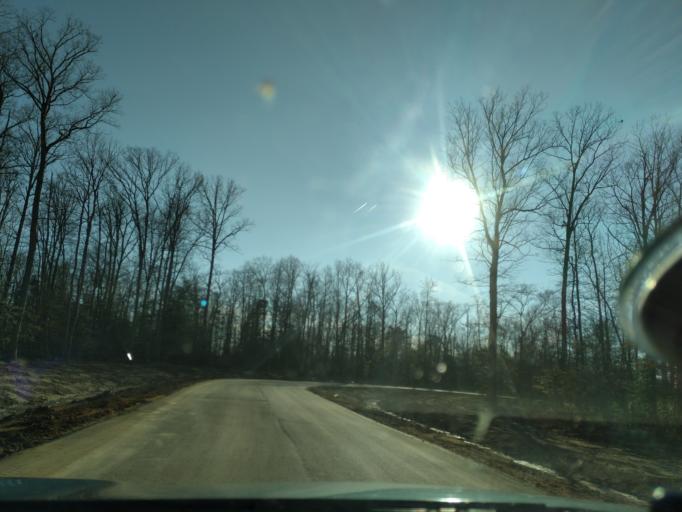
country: US
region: Maryland
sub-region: Charles County
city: La Plata
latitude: 38.4906
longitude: -76.8881
